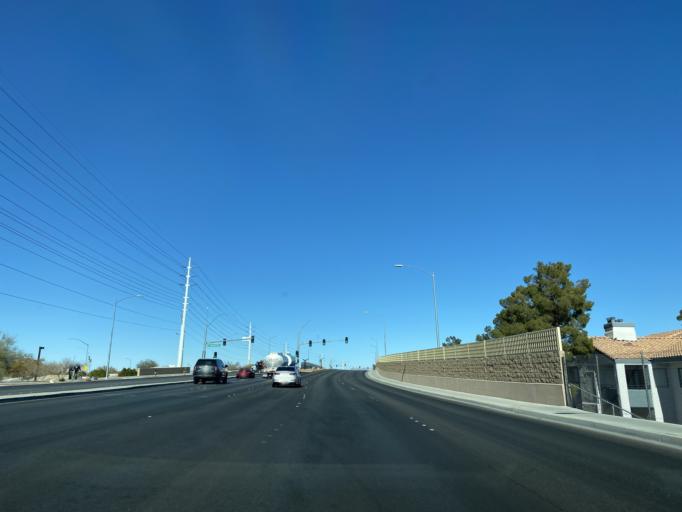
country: US
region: Nevada
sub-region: Clark County
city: Spring Valley
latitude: 36.1752
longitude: -115.2780
